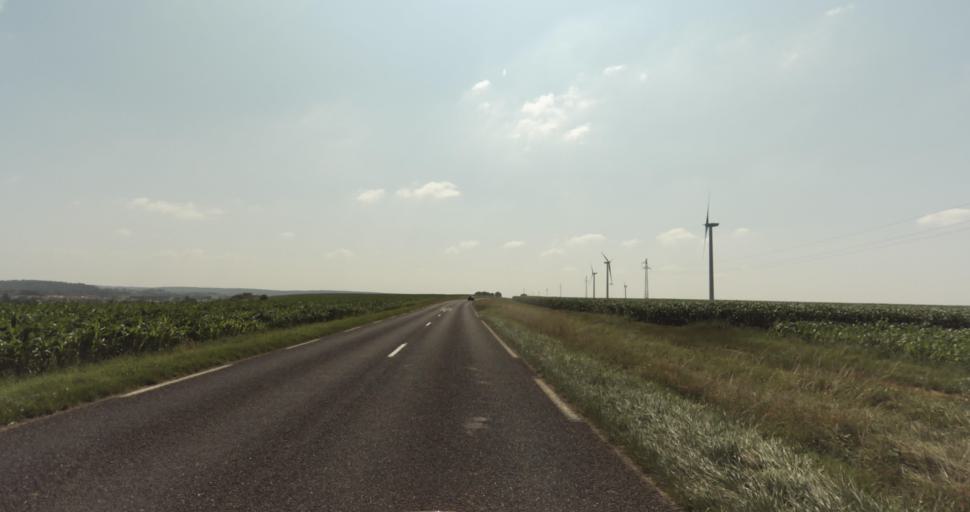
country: FR
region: Lorraine
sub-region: Departement de Meurthe-et-Moselle
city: Mancieulles
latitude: 49.2758
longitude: 5.8813
